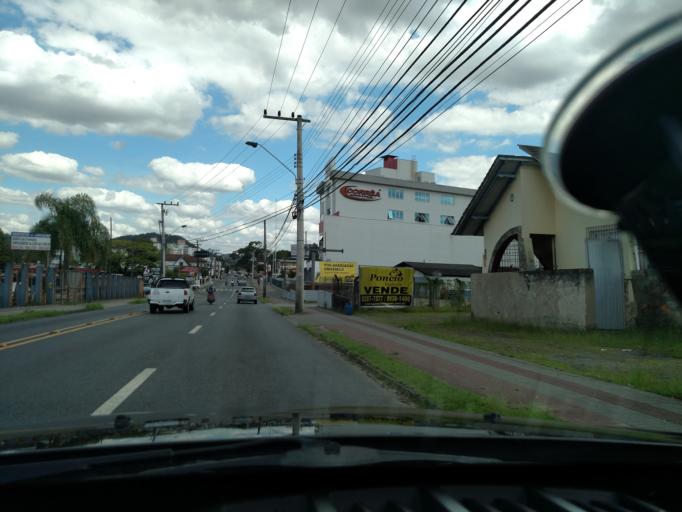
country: BR
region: Santa Catarina
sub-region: Blumenau
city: Blumenau
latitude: -26.8829
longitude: -49.0850
